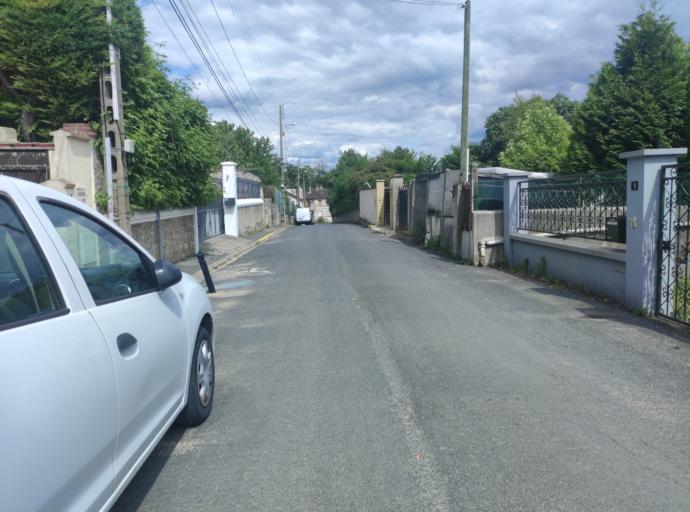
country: FR
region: Ile-de-France
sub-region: Departement de Seine-et-Marne
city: Meaux
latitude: 48.9556
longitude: 2.8679
